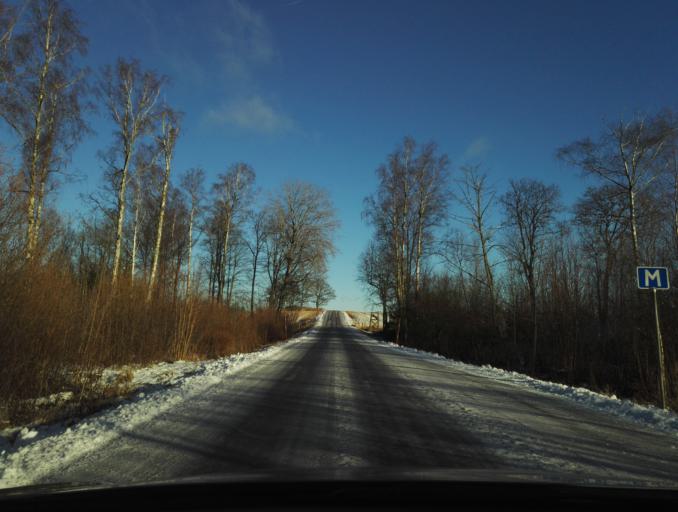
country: SE
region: Kronoberg
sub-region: Vaxjo Kommun
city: Gemla
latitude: 56.8372
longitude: 14.5934
